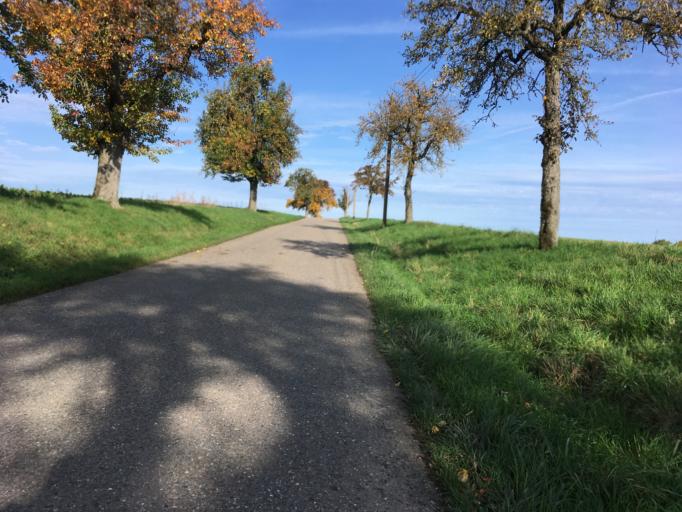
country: DE
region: Baden-Wuerttemberg
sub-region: Karlsruhe Region
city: Huffenhardt
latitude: 49.2698
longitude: 9.0471
